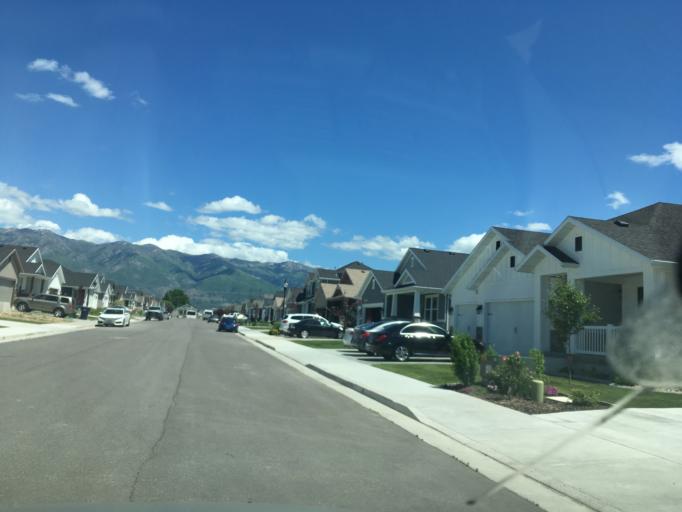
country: US
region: Utah
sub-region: Davis County
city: Layton
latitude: 41.0525
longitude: -112.0129
